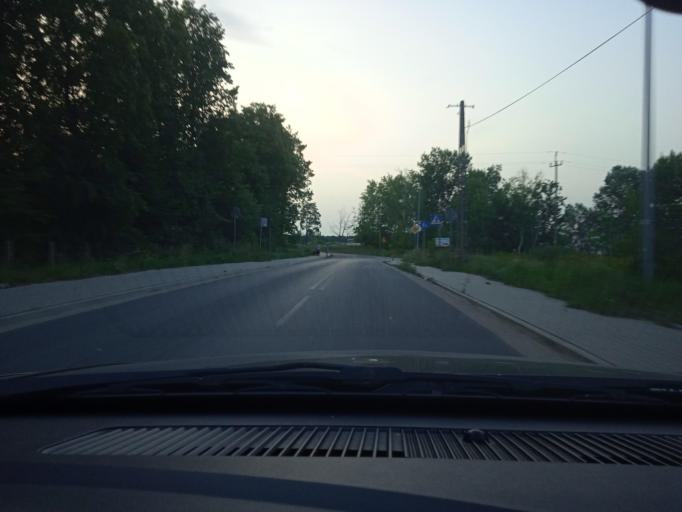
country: PL
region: Masovian Voivodeship
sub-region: Powiat nowodworski
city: Pomiechowek
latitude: 52.4667
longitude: 20.6960
